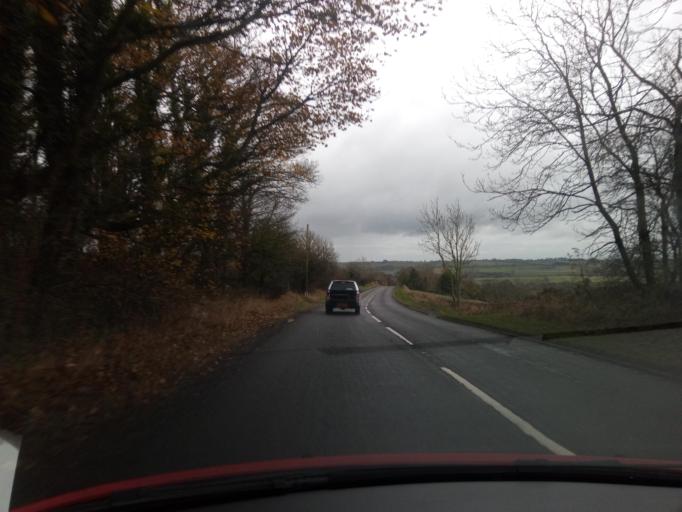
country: GB
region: England
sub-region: County Durham
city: Hamsterley
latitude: 54.6847
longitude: -1.7847
